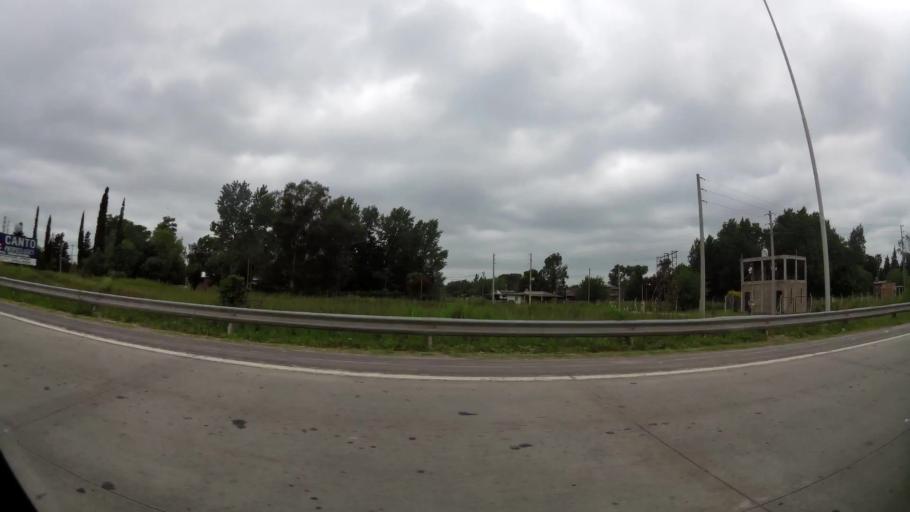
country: AR
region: Buenos Aires
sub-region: Partido de San Vicente
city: San Vicente
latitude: -35.0439
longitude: -58.4103
